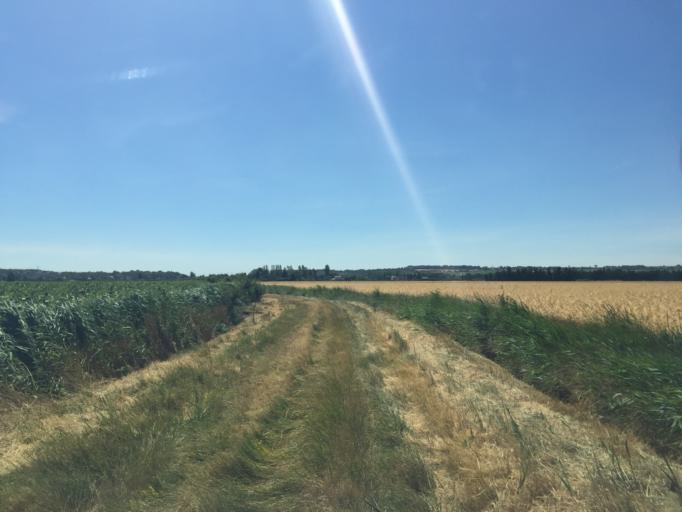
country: FR
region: Provence-Alpes-Cote d'Azur
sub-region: Departement du Vaucluse
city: Bedarrides
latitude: 44.0471
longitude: 4.9201
